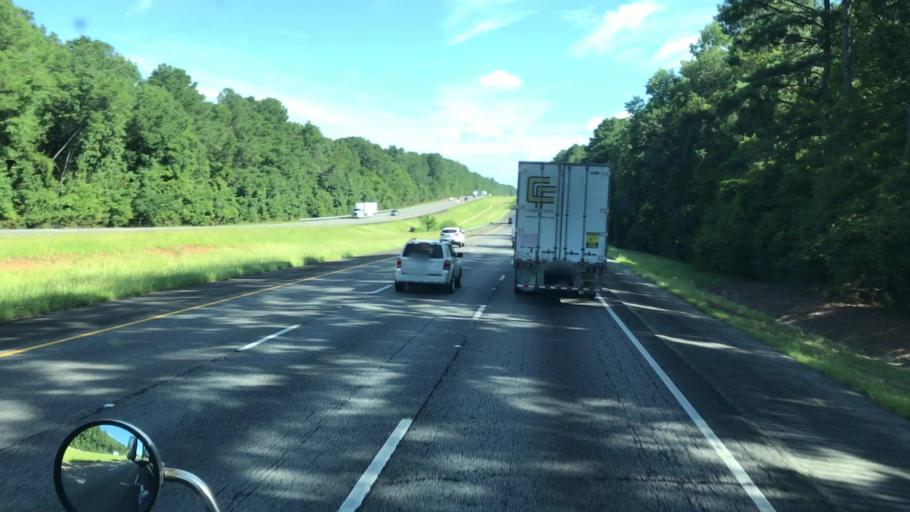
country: US
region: Georgia
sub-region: Houston County
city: Perry
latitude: 32.3632
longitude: -83.7681
